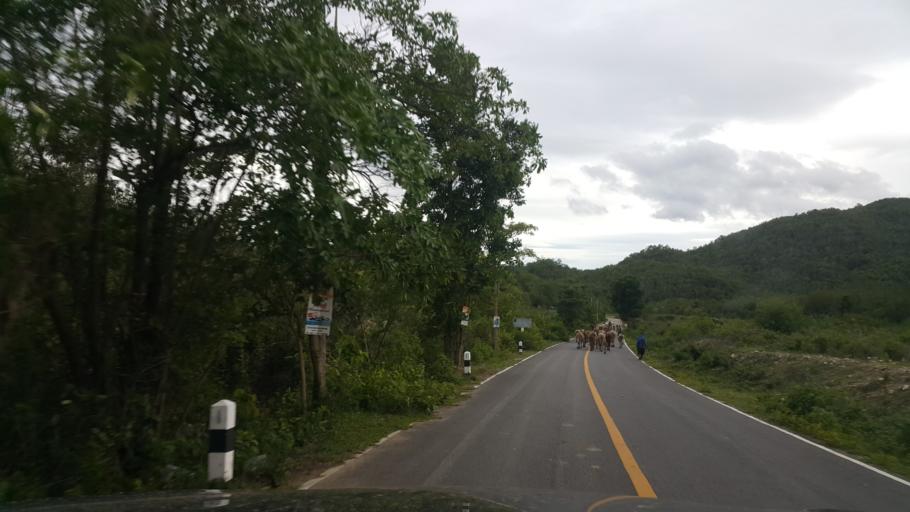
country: TH
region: Sukhothai
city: Thung Saliam
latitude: 17.1789
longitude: 99.4832
